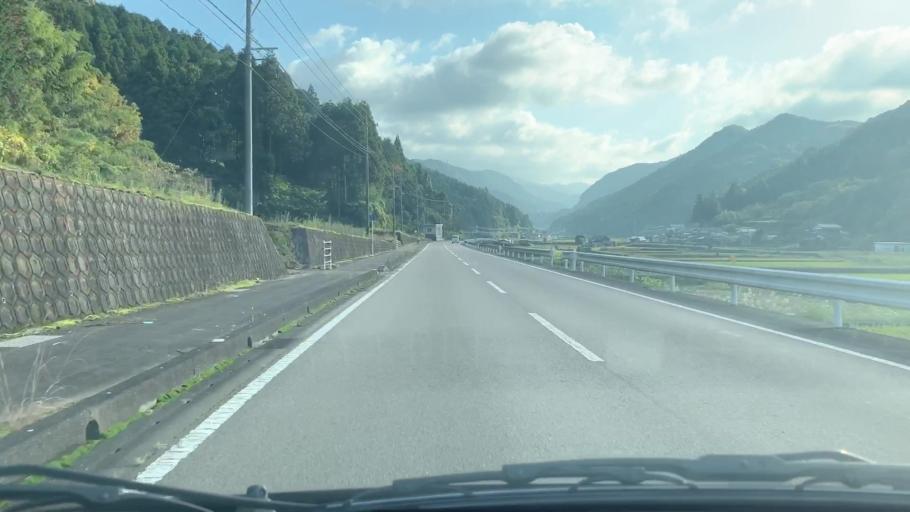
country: JP
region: Saga Prefecture
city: Kashima
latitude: 33.0688
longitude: 130.0701
